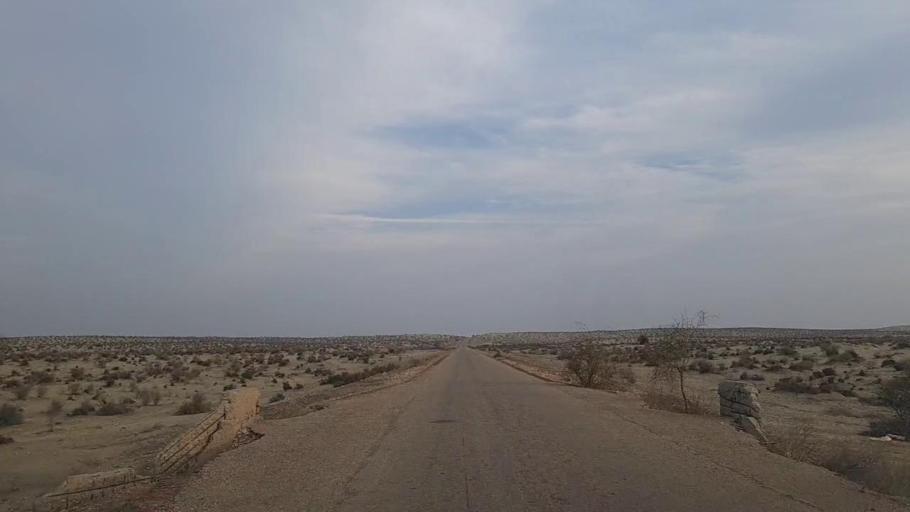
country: PK
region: Sindh
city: Daur
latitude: 26.5122
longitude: 68.5052
